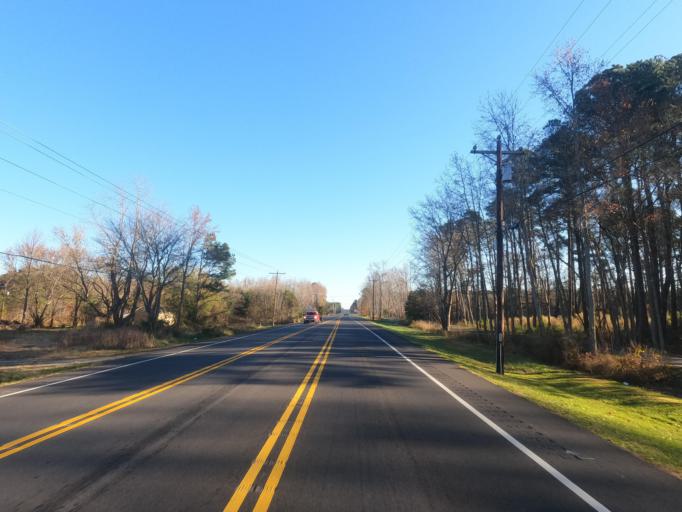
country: US
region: Maryland
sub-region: Somerset County
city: Crisfield
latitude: 38.0113
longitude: -75.8137
